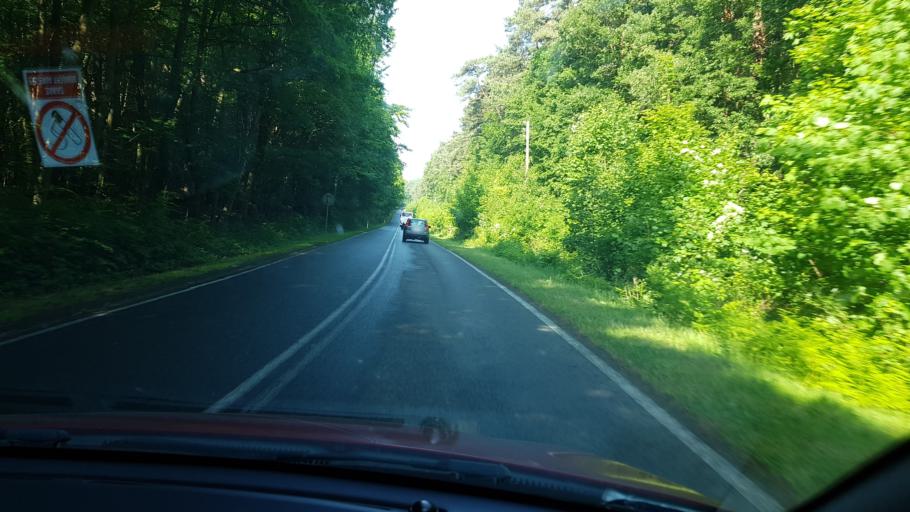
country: PL
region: West Pomeranian Voivodeship
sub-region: Powiat kamienski
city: Miedzyzdroje
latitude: 53.9663
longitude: 14.5577
